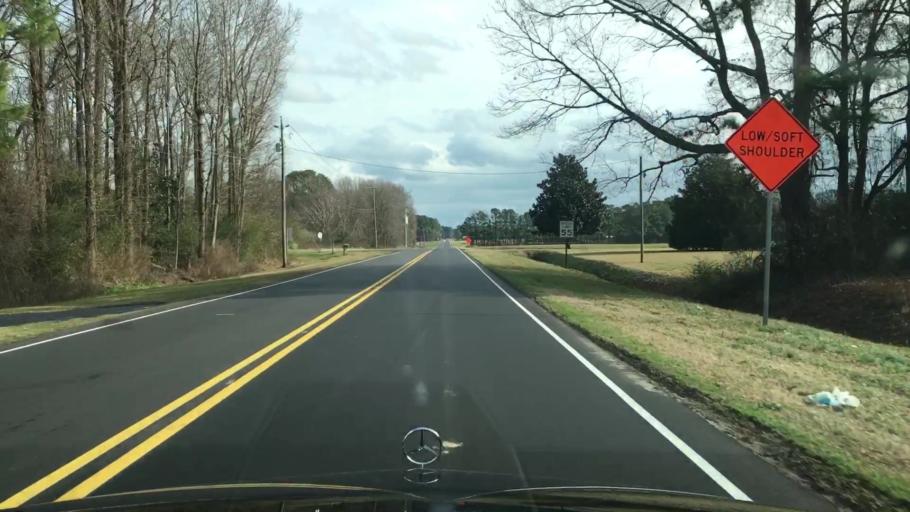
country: US
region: North Carolina
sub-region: Duplin County
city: Warsaw
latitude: 34.9807
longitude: -78.0324
